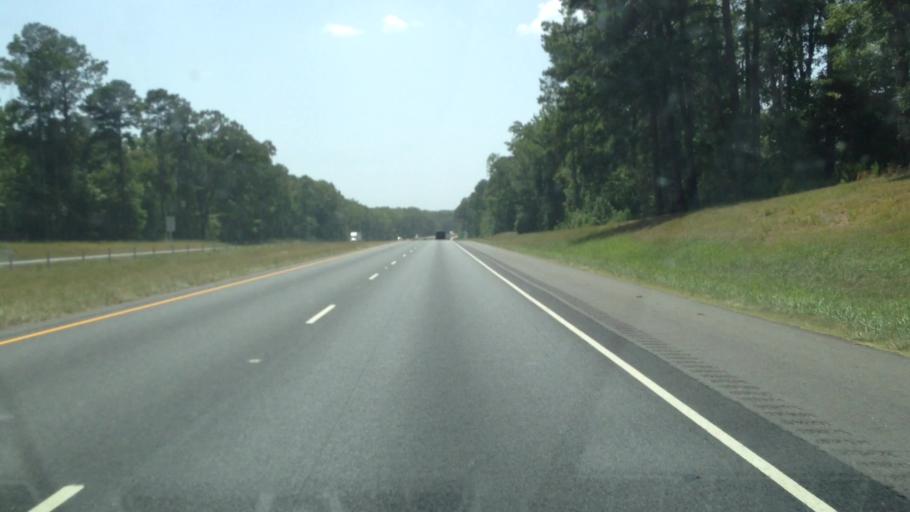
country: US
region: Louisiana
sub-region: Webster Parish
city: Minden
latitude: 32.5620
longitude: -93.1404
